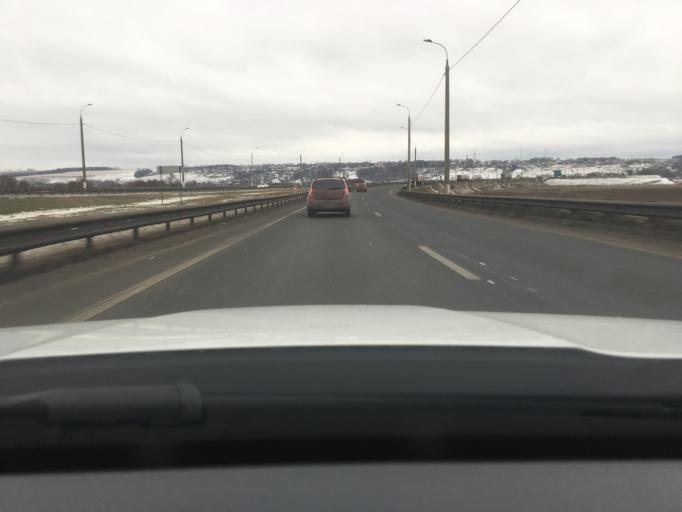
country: RU
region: Moskovskaya
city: Danki
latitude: 54.8669
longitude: 37.5019
